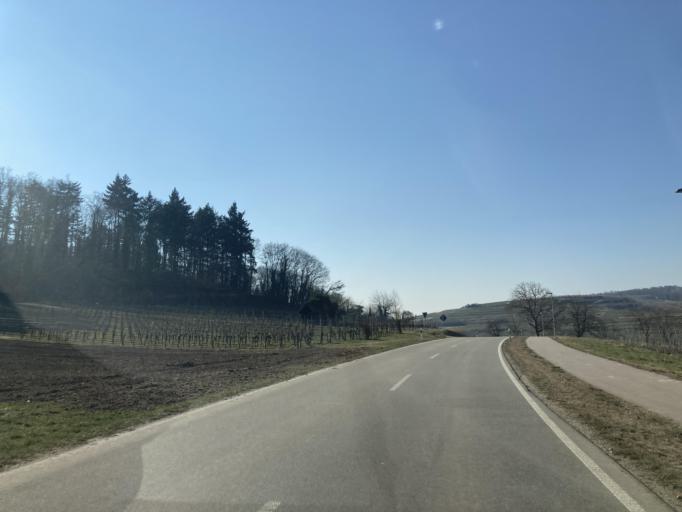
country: DE
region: Baden-Wuerttemberg
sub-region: Freiburg Region
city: Vogtsburg
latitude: 48.1051
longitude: 7.6192
